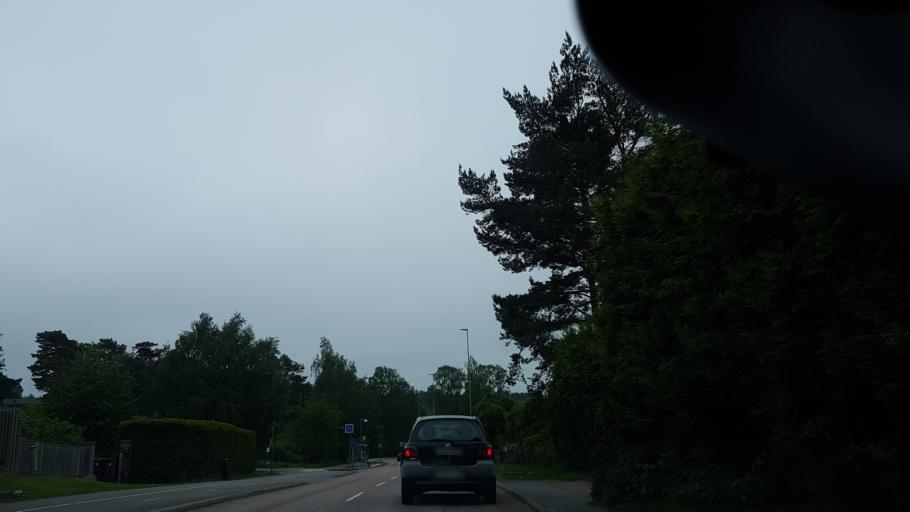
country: SE
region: Vaestra Goetaland
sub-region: Goteborg
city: Billdal
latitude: 57.6229
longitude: 11.9460
